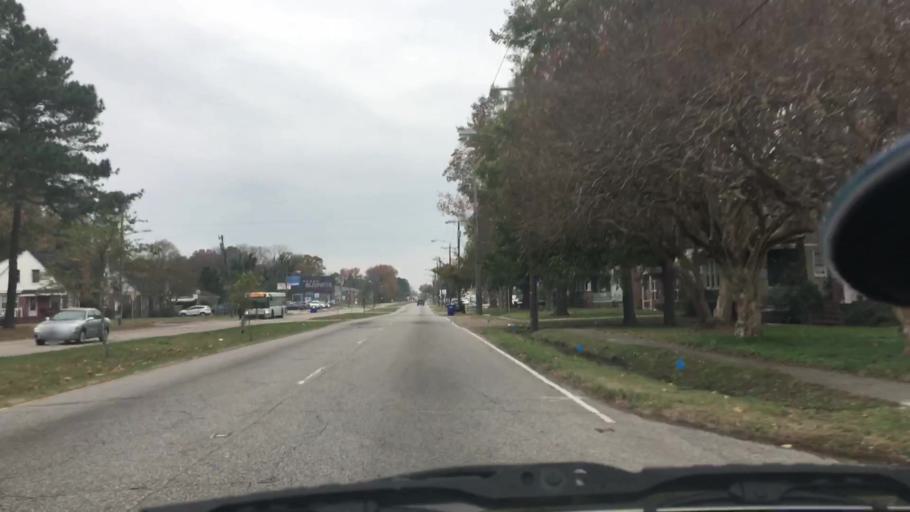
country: US
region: Virginia
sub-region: City of Norfolk
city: Norfolk
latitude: 36.8713
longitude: -76.2232
